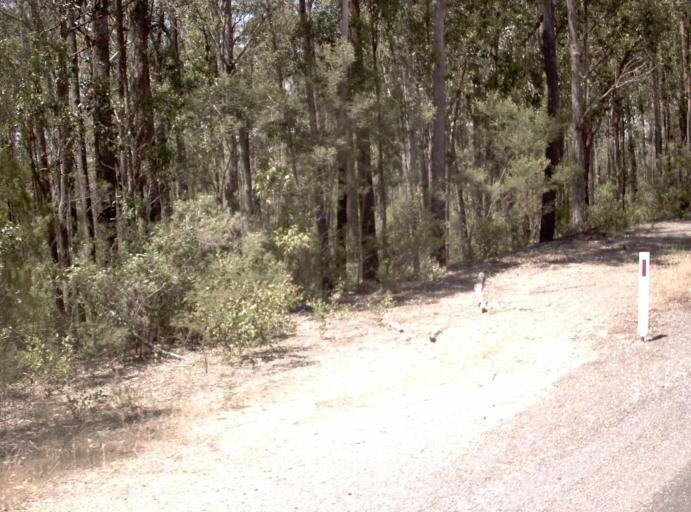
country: AU
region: Victoria
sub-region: East Gippsland
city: Lakes Entrance
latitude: -37.7058
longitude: 148.6504
